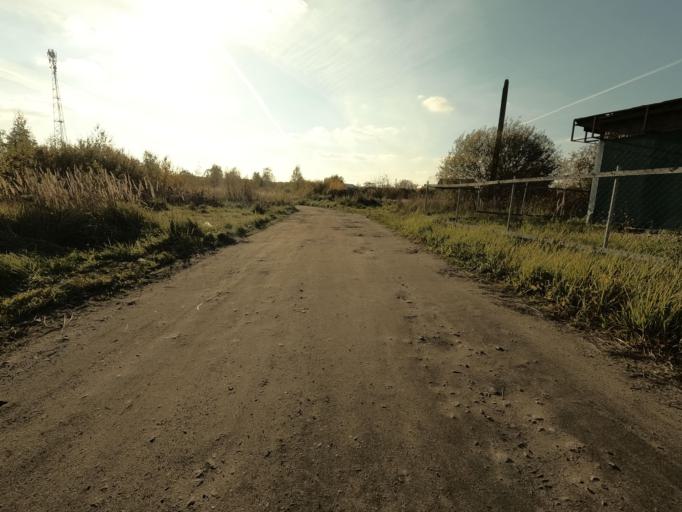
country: RU
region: Leningrad
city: Mga
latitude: 59.7473
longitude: 31.0628
